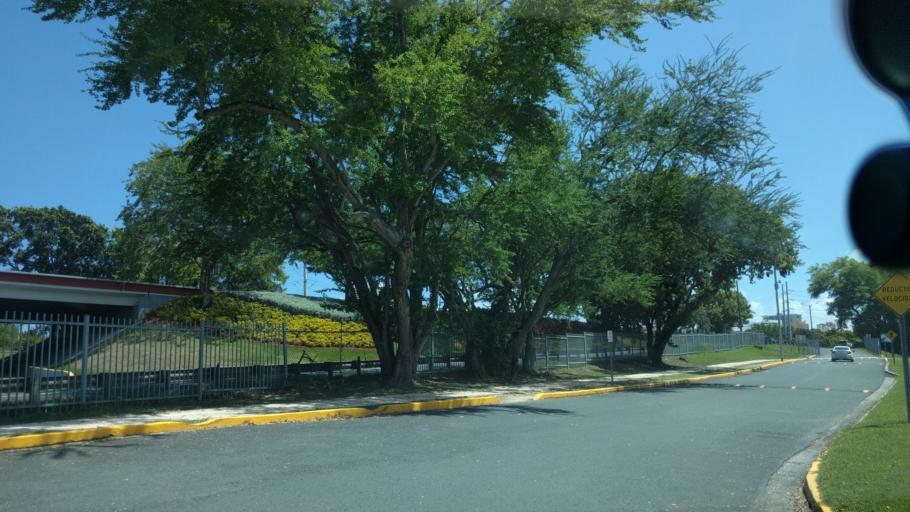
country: PR
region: San Juan
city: San Juan
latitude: 18.4422
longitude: -66.0783
